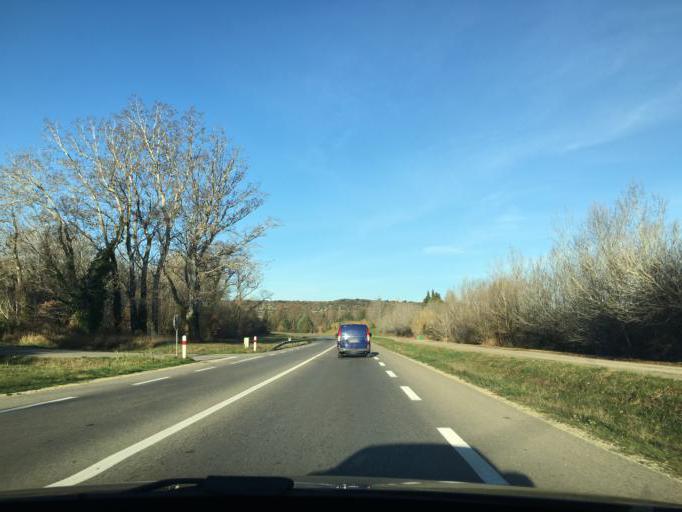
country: FR
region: Provence-Alpes-Cote d'Azur
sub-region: Departement du Vaucluse
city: Caumont-sur-Durance
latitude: 43.8852
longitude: 4.9473
